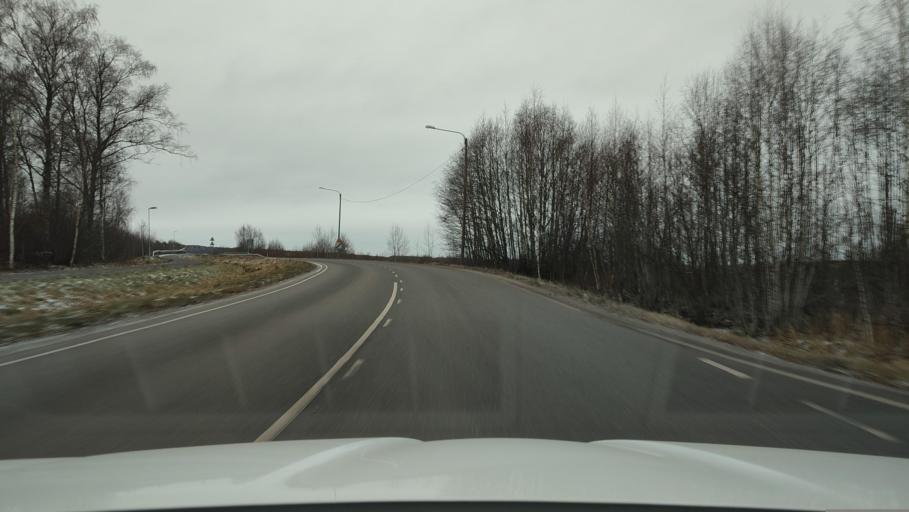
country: FI
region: Ostrobothnia
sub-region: Vaasa
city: Ristinummi
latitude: 63.0366
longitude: 21.7820
